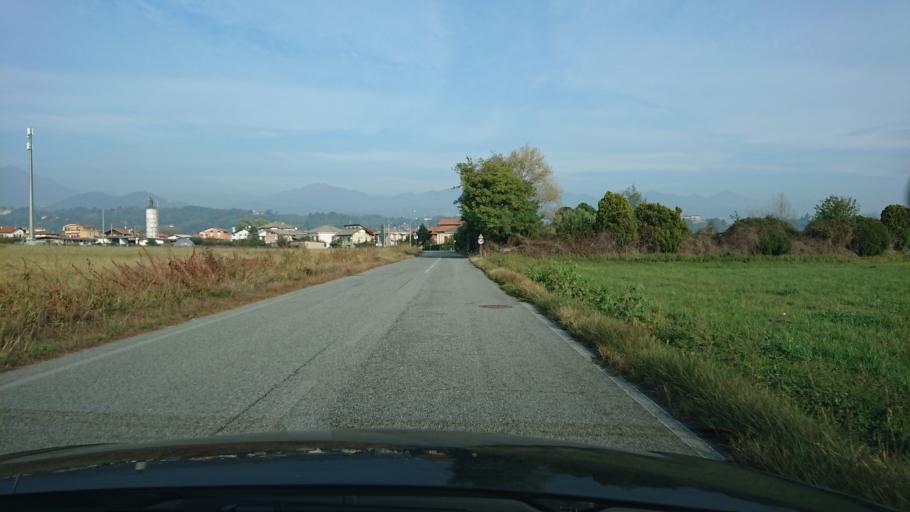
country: IT
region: Piedmont
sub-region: Provincia di Biella
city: Valdengo
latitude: 45.5575
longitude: 8.1330
